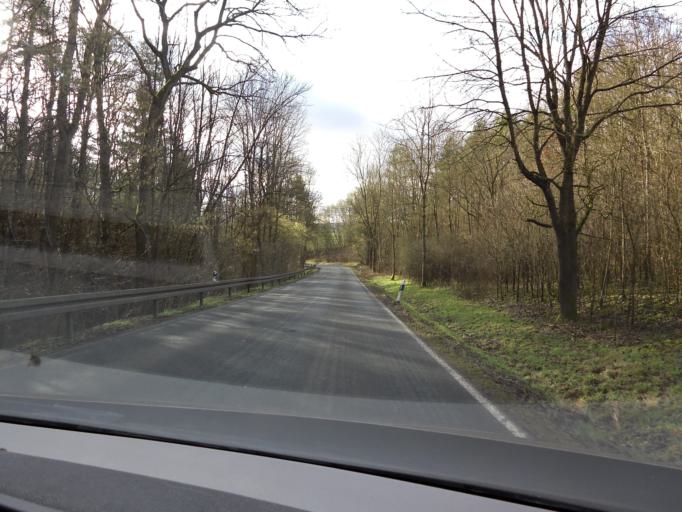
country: DE
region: Thuringia
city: Creuzburg
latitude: 51.0616
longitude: 10.2338
